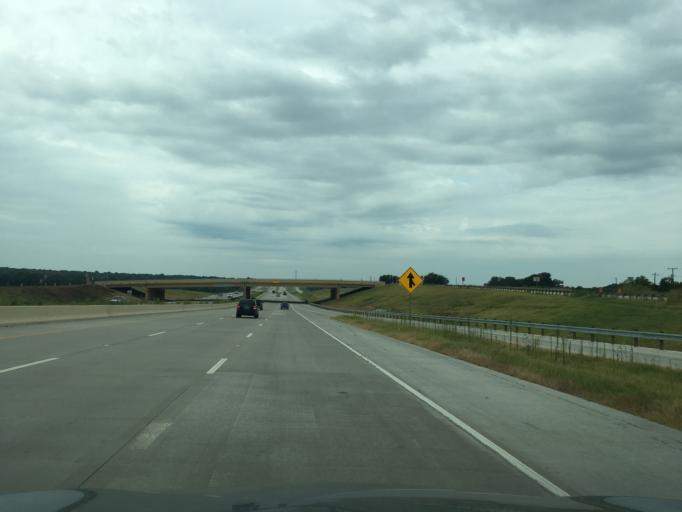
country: US
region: Texas
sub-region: Collin County
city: Melissa
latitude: 33.3117
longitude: -96.5910
